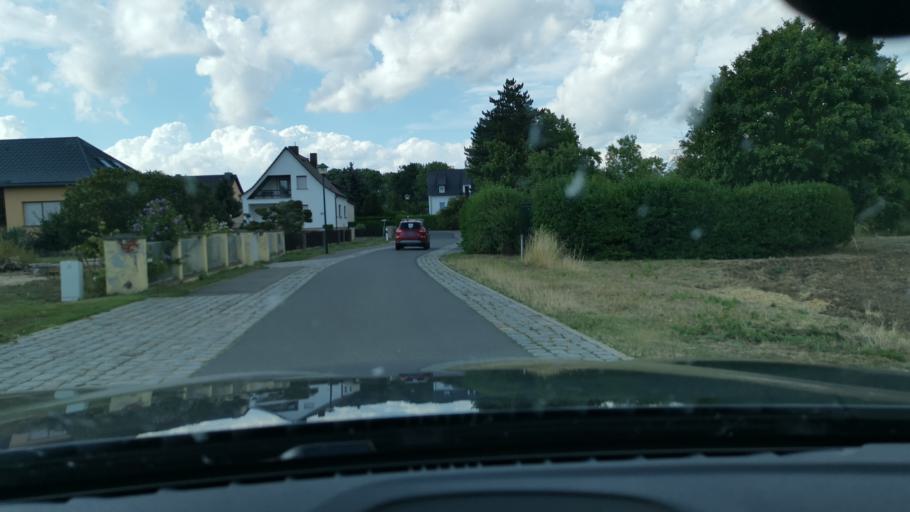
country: DE
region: Saxony
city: Zschepplin
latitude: 51.4813
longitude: 12.6181
